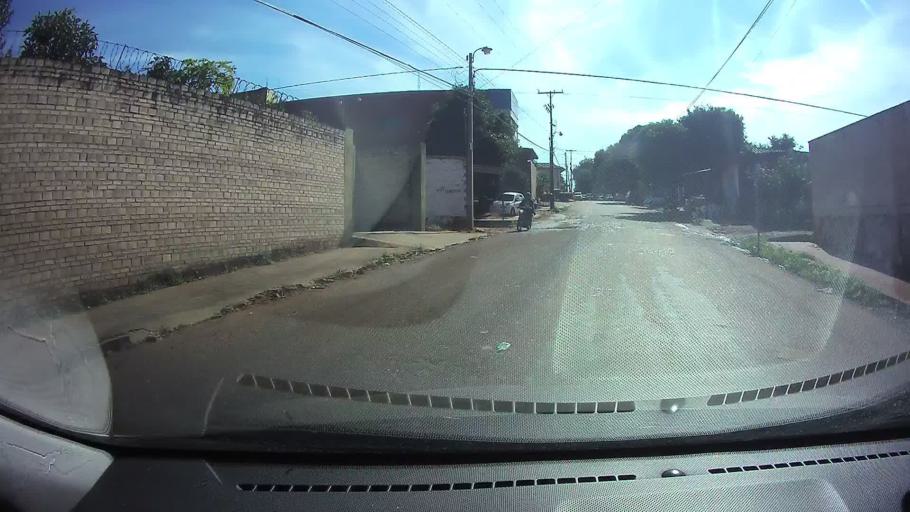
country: PY
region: Central
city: Villa Elisa
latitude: -25.3593
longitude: -57.5696
